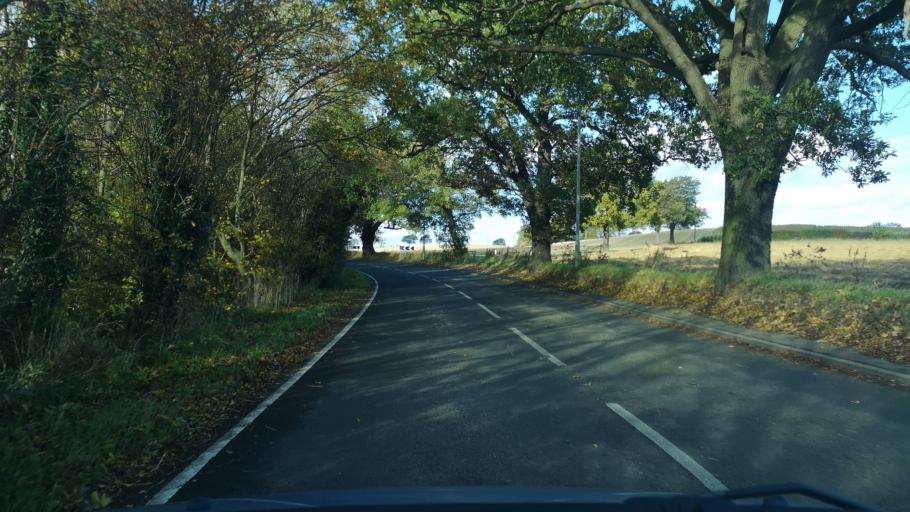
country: GB
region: England
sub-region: City and Borough of Wakefield
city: Low Ackworth
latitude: 53.6599
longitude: -1.3402
